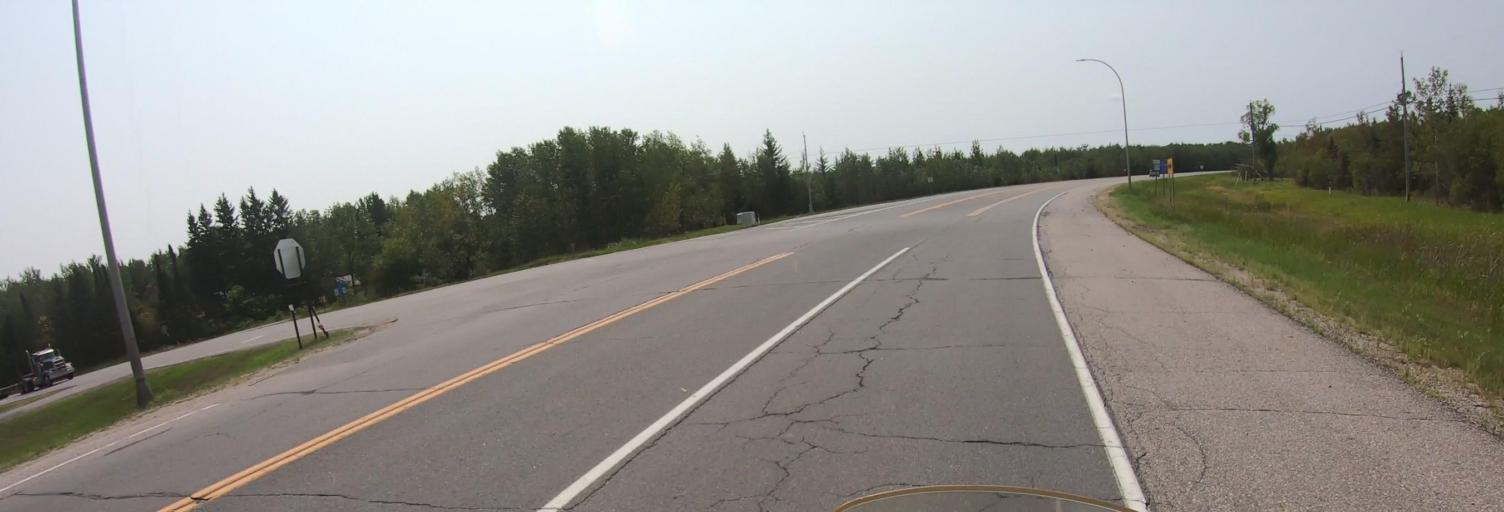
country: US
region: Minnesota
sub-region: Koochiching County
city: International Falls
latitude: 48.5558
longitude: -93.4407
